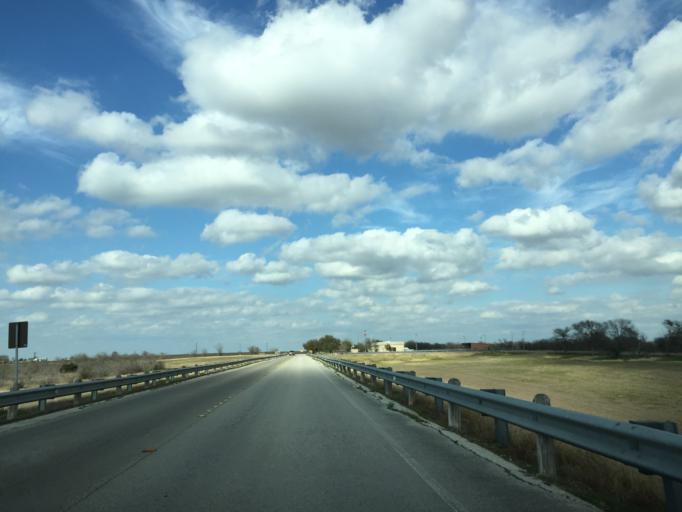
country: US
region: Texas
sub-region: Williamson County
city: Granger
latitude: 30.7157
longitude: -97.3230
